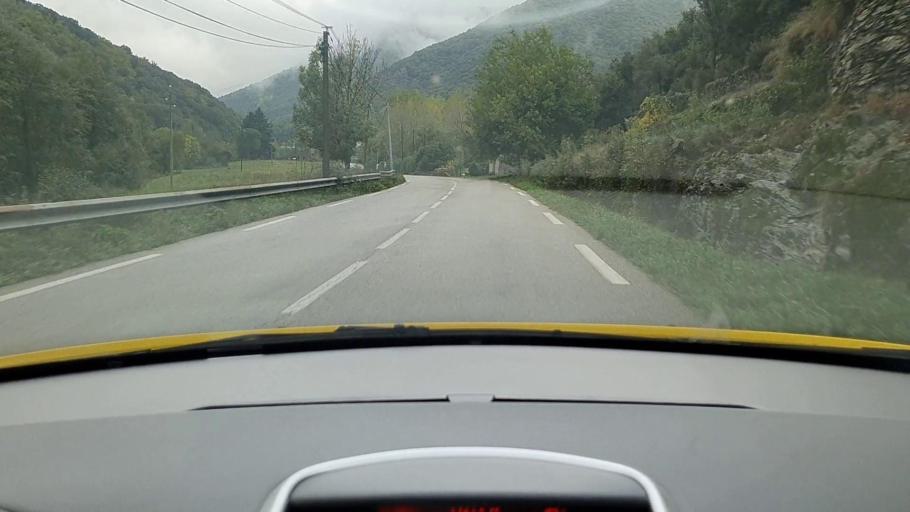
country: FR
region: Languedoc-Roussillon
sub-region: Departement du Gard
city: Valleraugue
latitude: 44.0829
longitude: 3.6202
